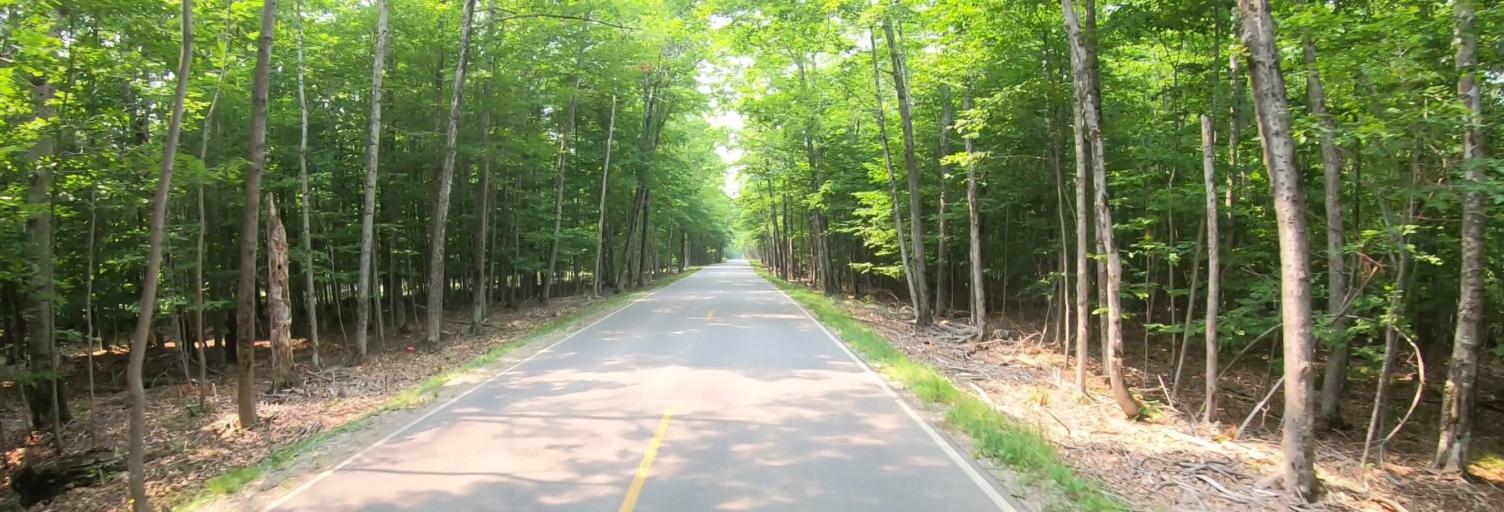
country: CA
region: Ontario
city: Thessalon
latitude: 46.0132
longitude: -83.7009
